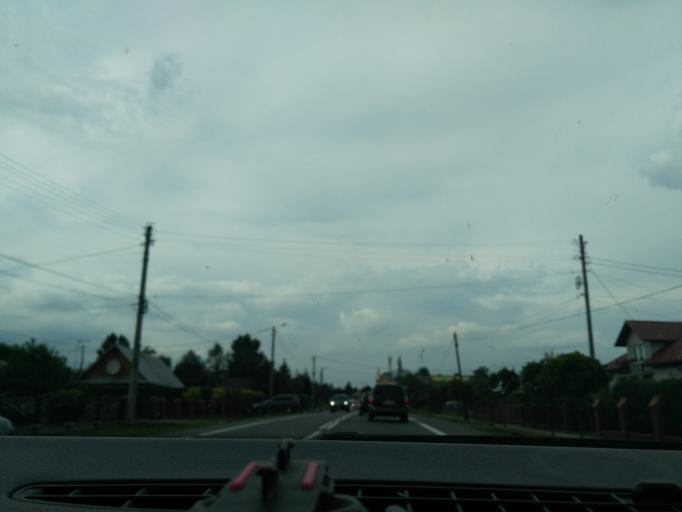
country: PL
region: Subcarpathian Voivodeship
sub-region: Powiat rzeszowski
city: Kamien
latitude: 50.3244
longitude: 22.1374
